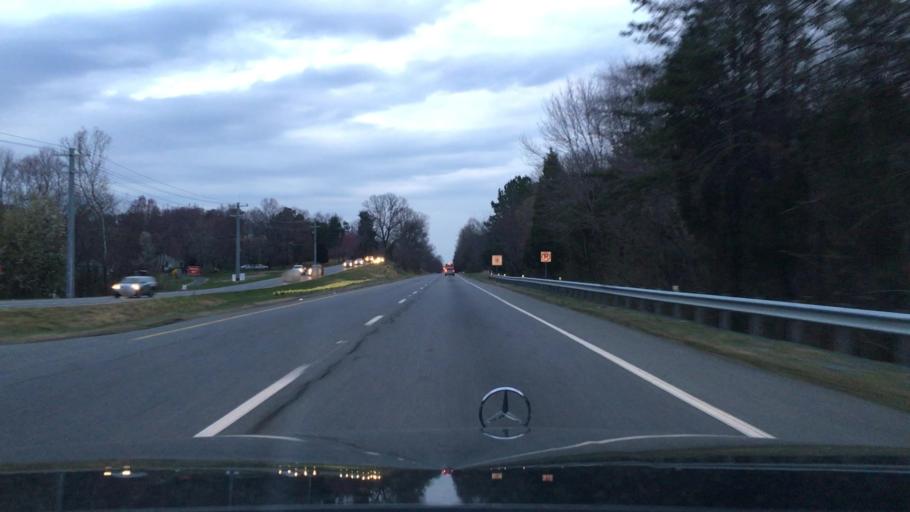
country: US
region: Virginia
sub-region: Albemarle County
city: Hollymead
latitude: 38.1709
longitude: -78.4101
